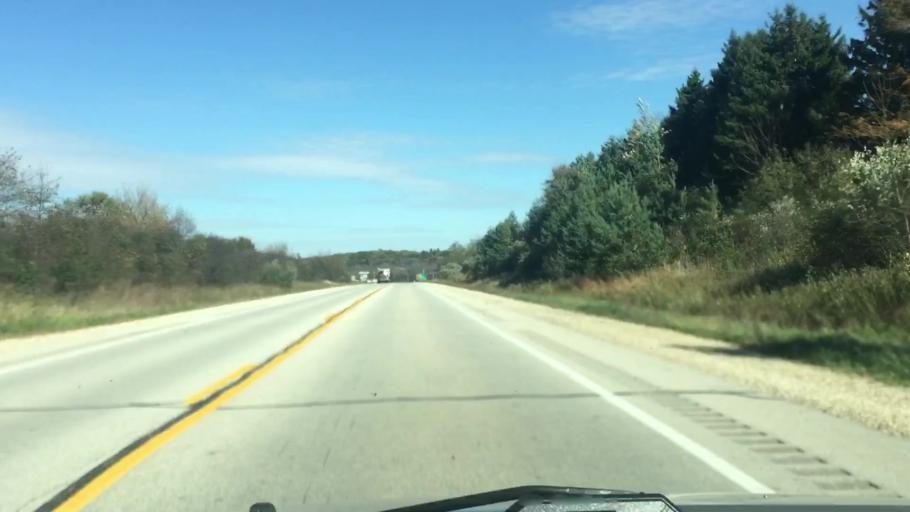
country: US
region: Wisconsin
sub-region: Waukesha County
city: North Prairie
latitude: 42.9529
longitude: -88.3661
